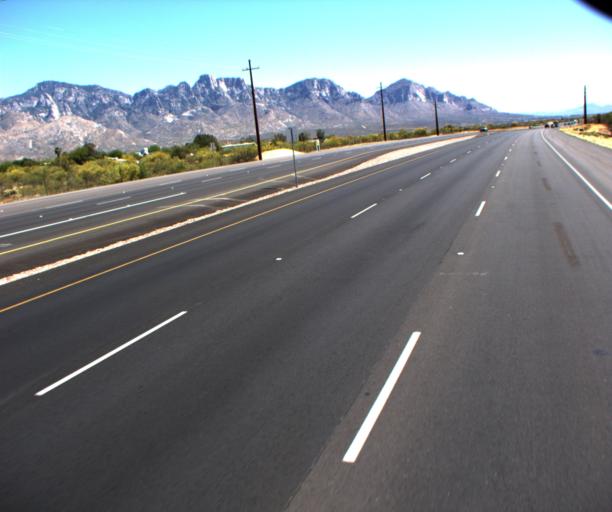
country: US
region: Arizona
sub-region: Pima County
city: Catalina
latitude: 32.4628
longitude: -110.9273
